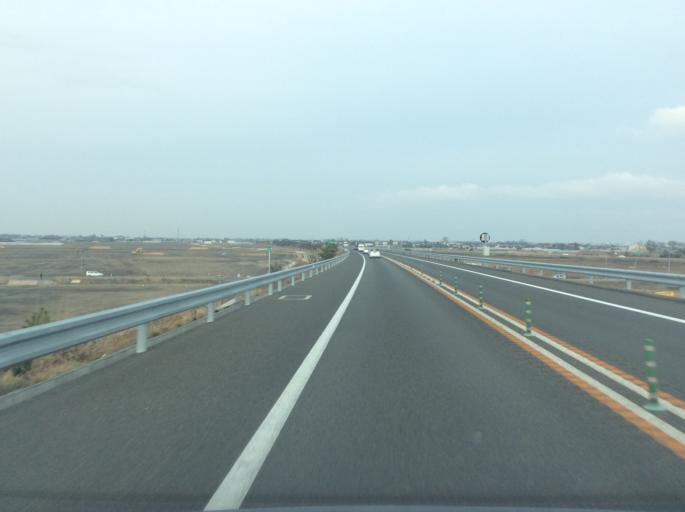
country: JP
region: Miyagi
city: Watari
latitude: 38.0173
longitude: 140.8868
